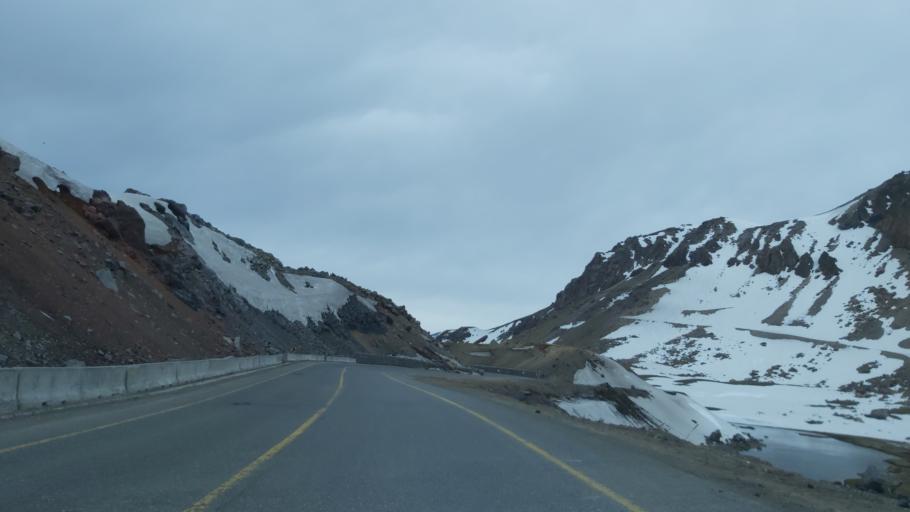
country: CL
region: Maule
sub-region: Provincia de Linares
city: Colbun
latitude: -36.0053
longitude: -70.5585
